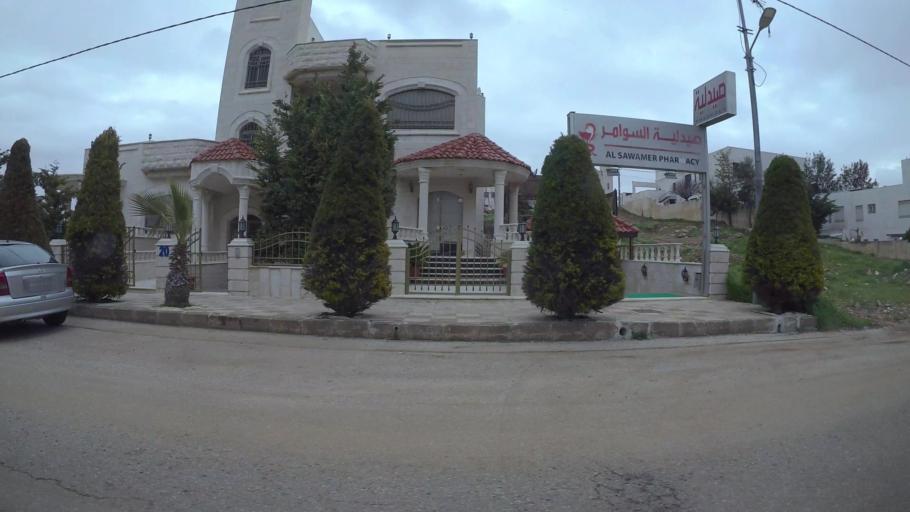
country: JO
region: Amman
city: Al Jubayhah
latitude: 31.9920
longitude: 35.8410
